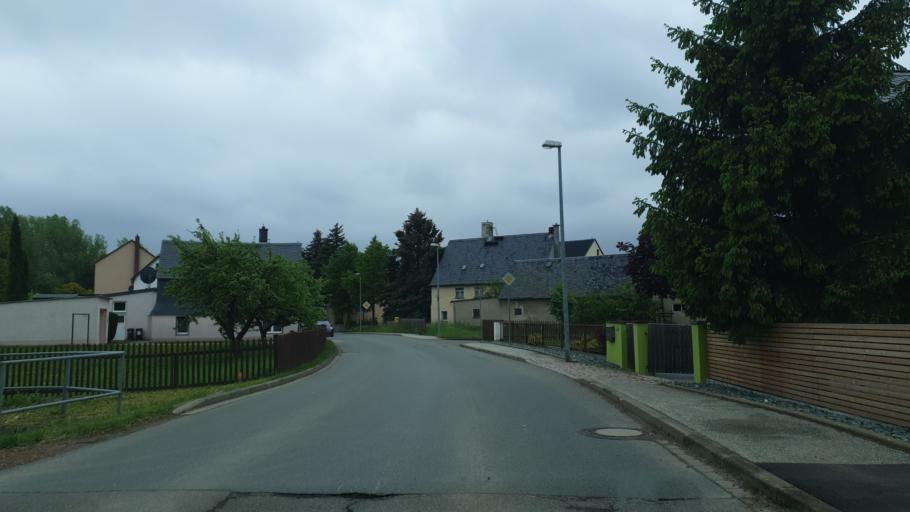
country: DE
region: Saxony
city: Hartmannsdorf
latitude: 50.8592
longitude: 12.8075
